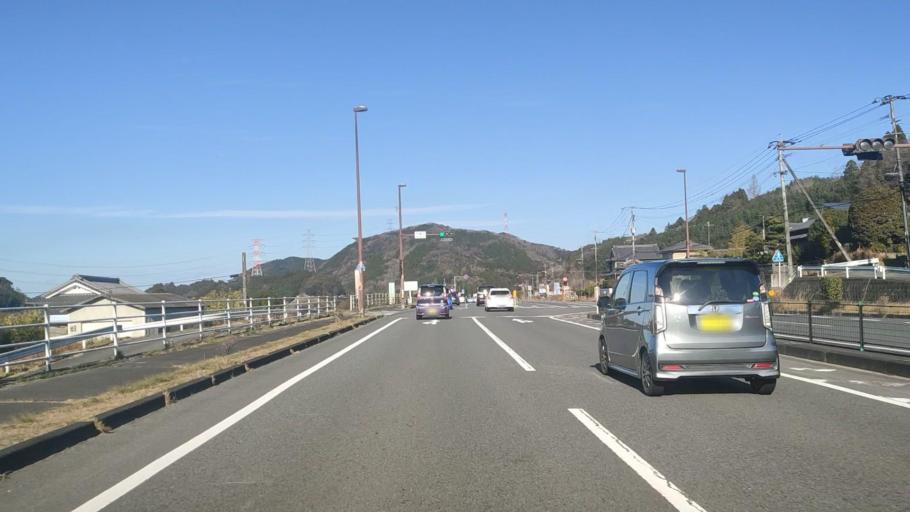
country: JP
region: Oita
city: Oita
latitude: 33.1021
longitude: 131.6520
